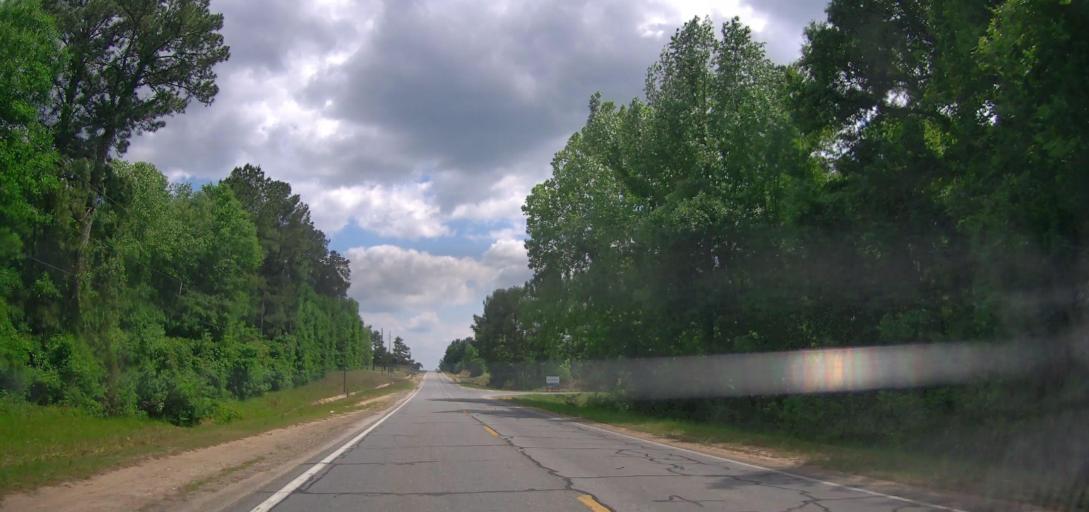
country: US
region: Georgia
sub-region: Laurens County
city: East Dublin
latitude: 32.5147
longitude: -82.8423
